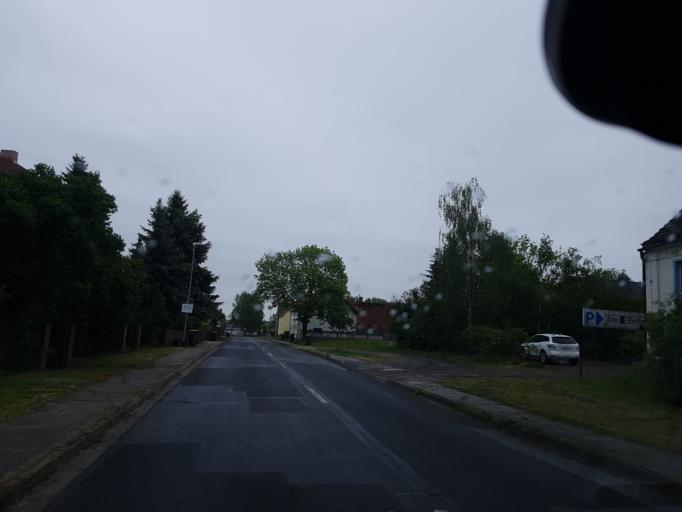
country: DE
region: Brandenburg
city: Cottbus
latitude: 51.6782
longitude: 14.3593
